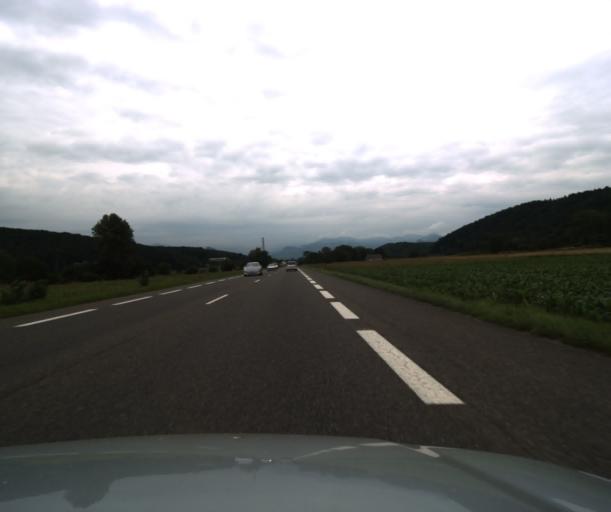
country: FR
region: Midi-Pyrenees
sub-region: Departement des Hautes-Pyrenees
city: Ossun
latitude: 43.1529
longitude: -0.0218
